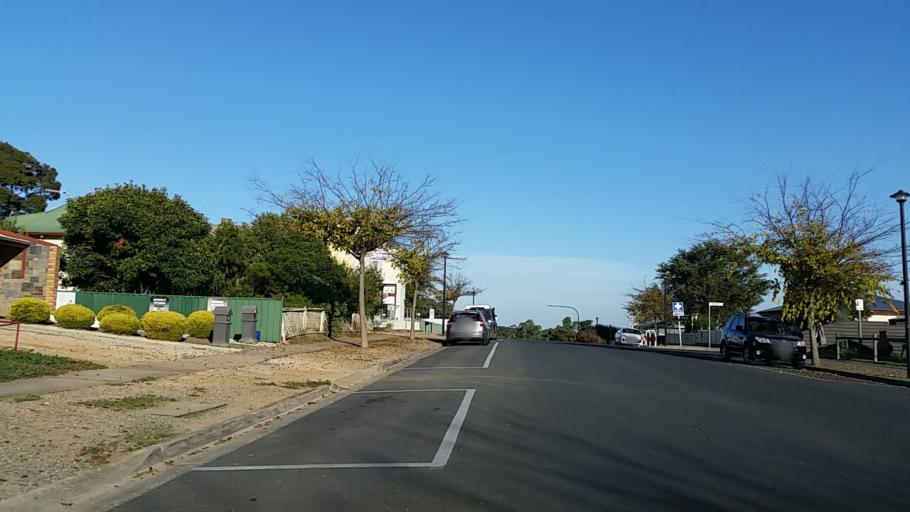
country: AU
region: South Australia
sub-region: Alexandrina
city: Strathalbyn
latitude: -35.2563
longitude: 138.8936
